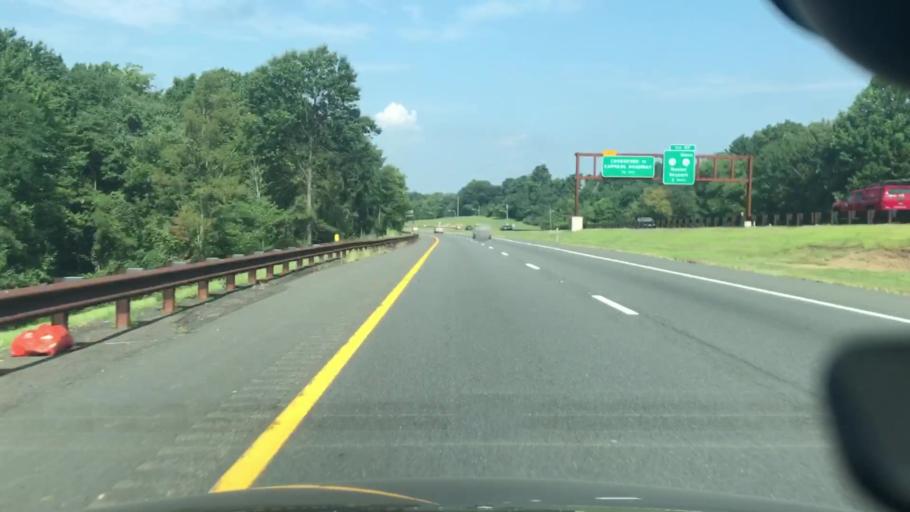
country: US
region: New Jersey
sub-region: Monmouth County
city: Strathmore
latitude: 40.3949
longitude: -74.1828
